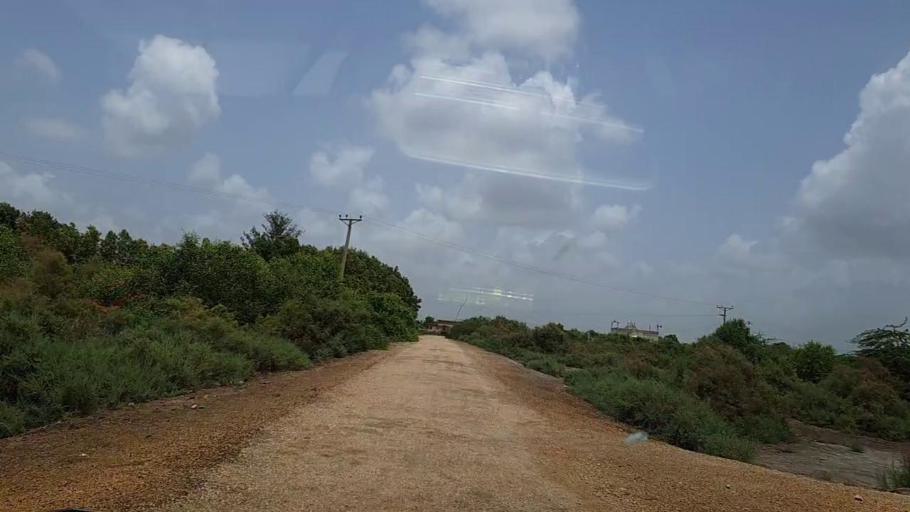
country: PK
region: Sindh
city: Keti Bandar
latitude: 24.1656
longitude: 67.5441
